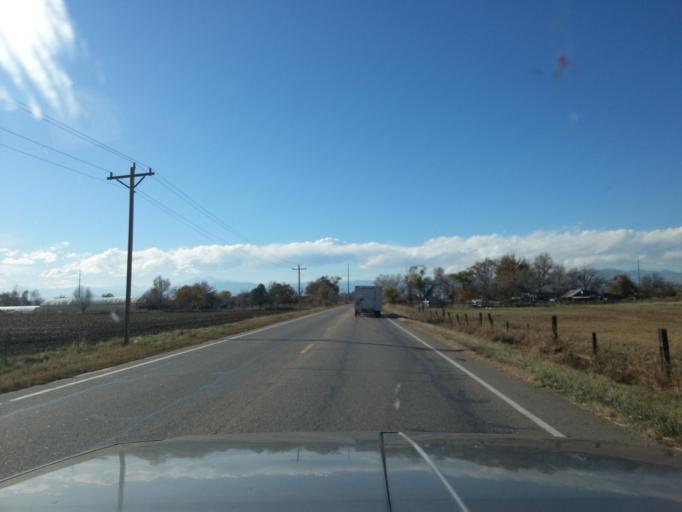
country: US
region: Colorado
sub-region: Larimer County
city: Loveland
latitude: 40.3783
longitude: -105.0334
